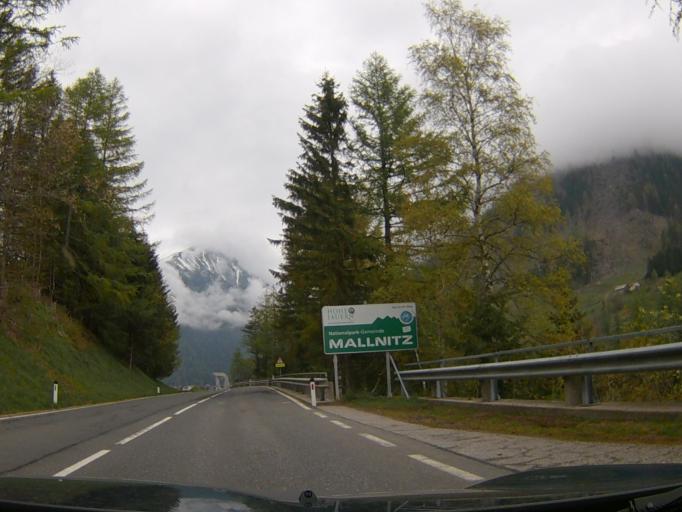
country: AT
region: Carinthia
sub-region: Politischer Bezirk Spittal an der Drau
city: Obervellach
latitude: 46.9718
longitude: 13.1813
